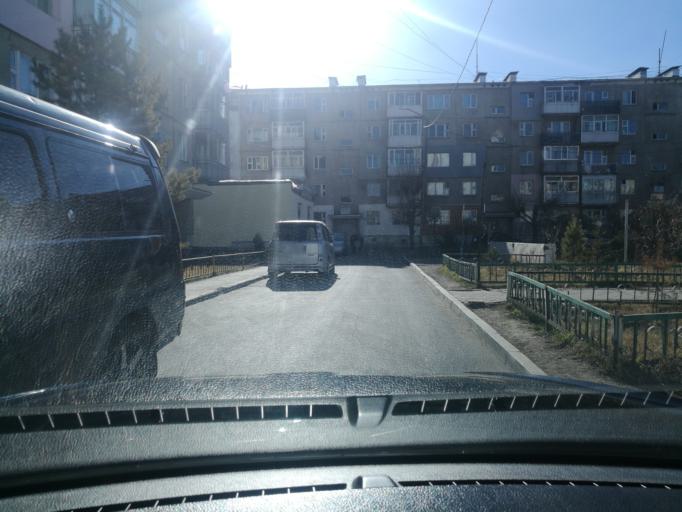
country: MN
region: Ulaanbaatar
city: Ulaanbaatar
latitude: 47.9034
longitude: 106.9057
